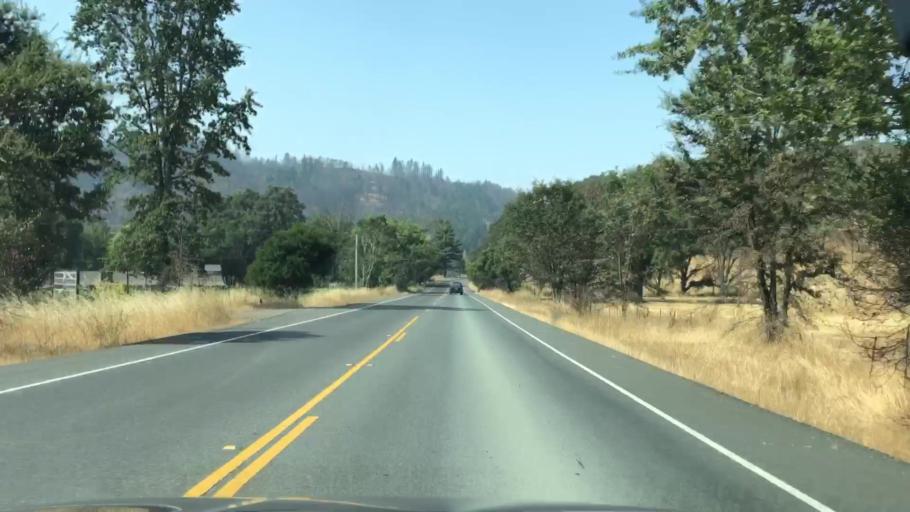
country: US
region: California
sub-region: Sonoma County
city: Larkfield-Wikiup
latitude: 38.5529
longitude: -122.6999
